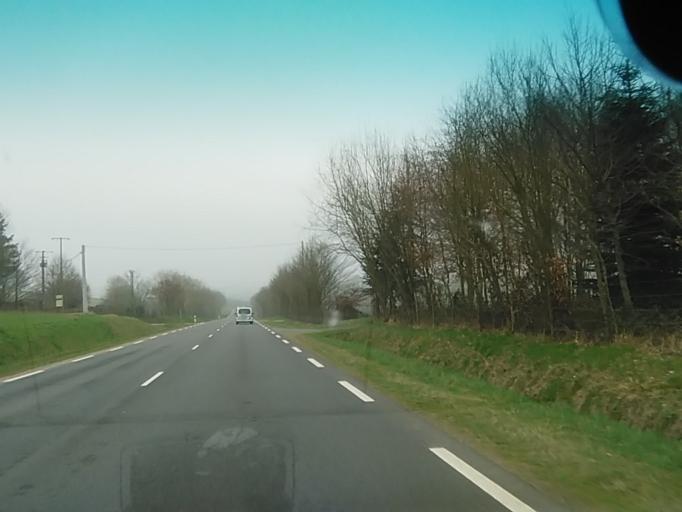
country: FR
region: Lower Normandy
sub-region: Departement de l'Orne
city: Magny-le-Desert
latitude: 48.6182
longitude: -0.2891
